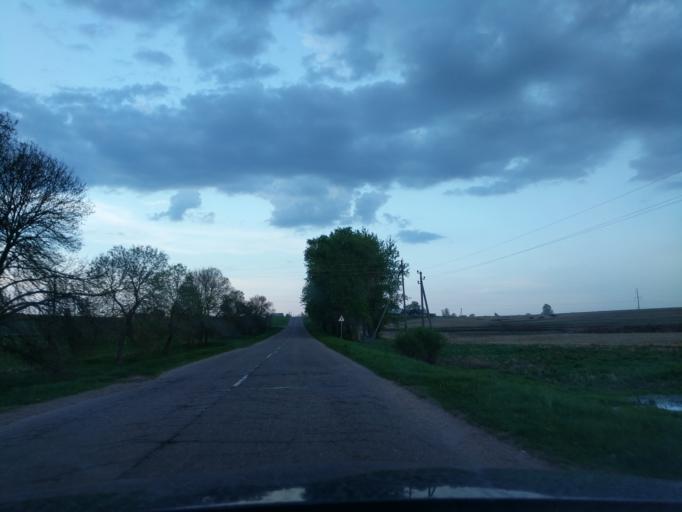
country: BY
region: Minsk
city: Novy Svyerzhan'
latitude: 53.4750
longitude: 26.6339
